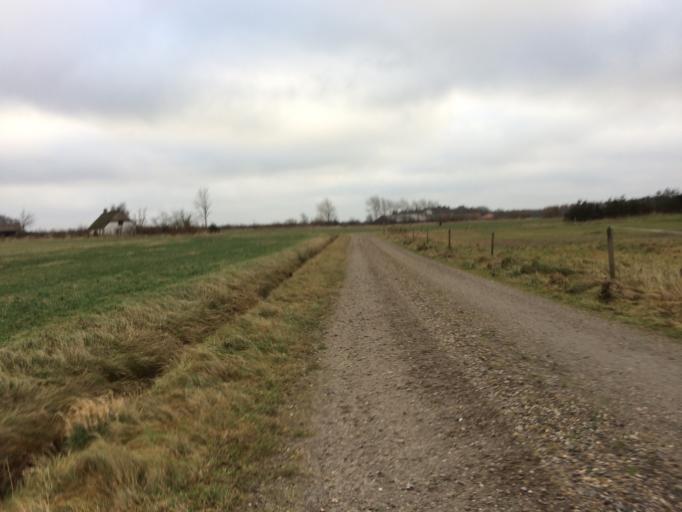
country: DK
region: Central Jutland
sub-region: Holstebro Kommune
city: Ulfborg
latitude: 56.2639
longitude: 8.2510
